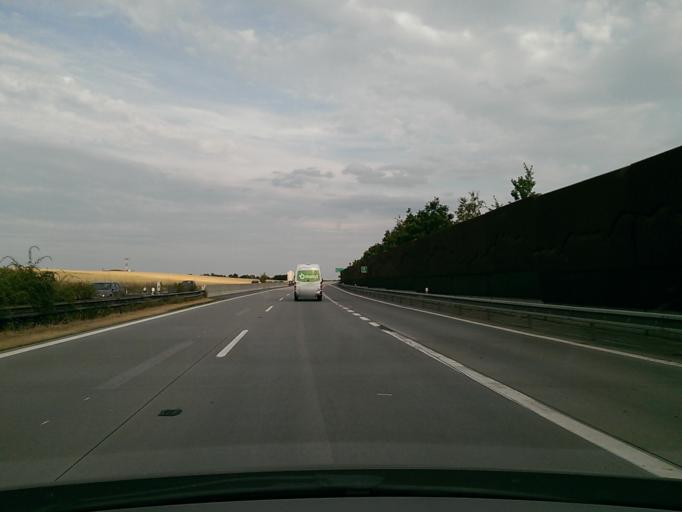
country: CZ
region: Vysocina
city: Merin
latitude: 49.3964
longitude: 15.8868
